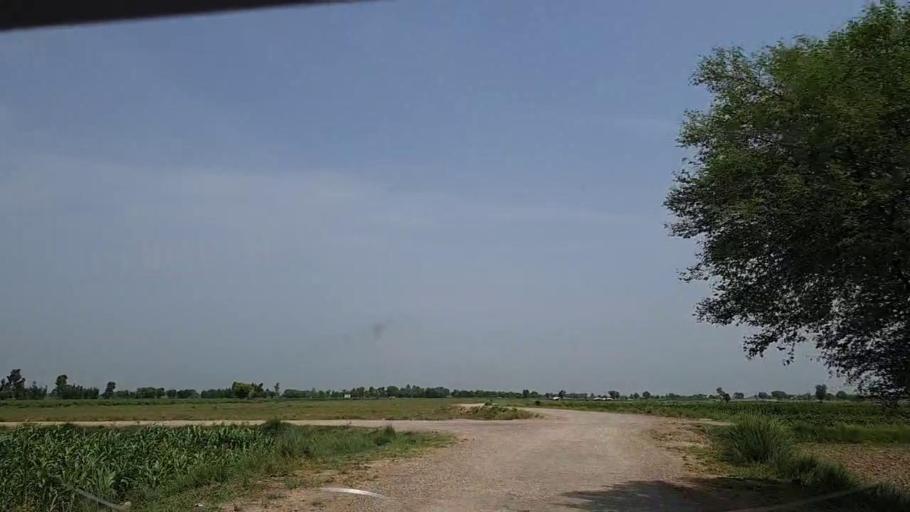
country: PK
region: Sindh
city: Tharu Shah
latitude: 26.9116
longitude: 68.0530
